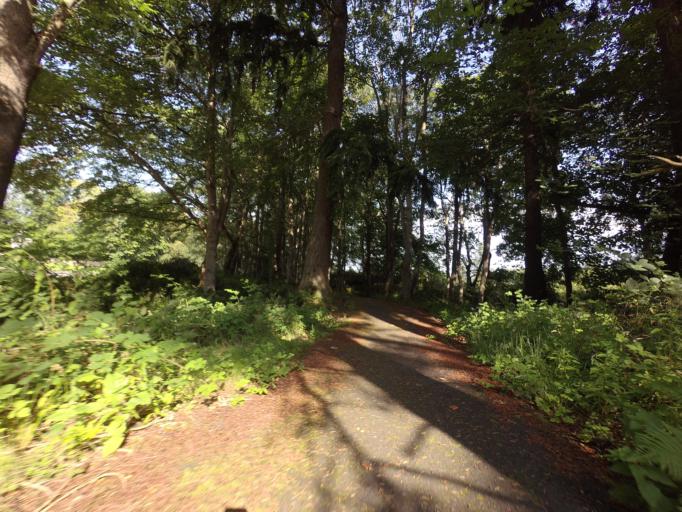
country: GB
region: Scotland
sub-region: Highland
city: Evanton
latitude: 57.6760
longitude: -4.3134
